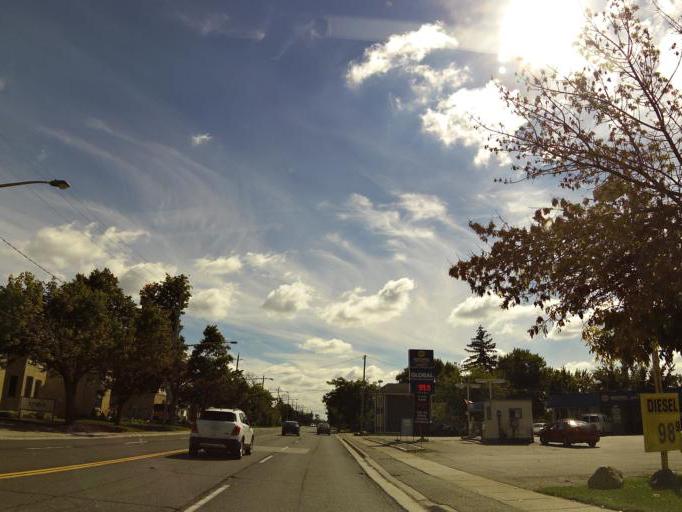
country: CA
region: Ontario
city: London
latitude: 42.9069
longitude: -81.2988
